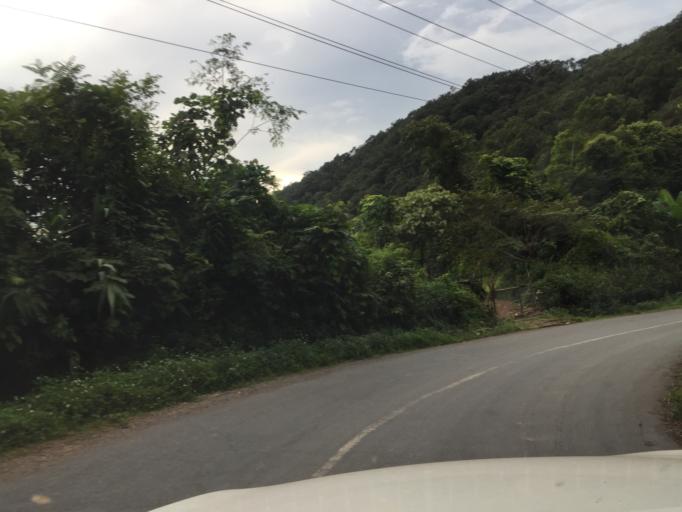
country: LA
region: Phongsali
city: Phongsali
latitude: 21.3369
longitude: 102.0471
